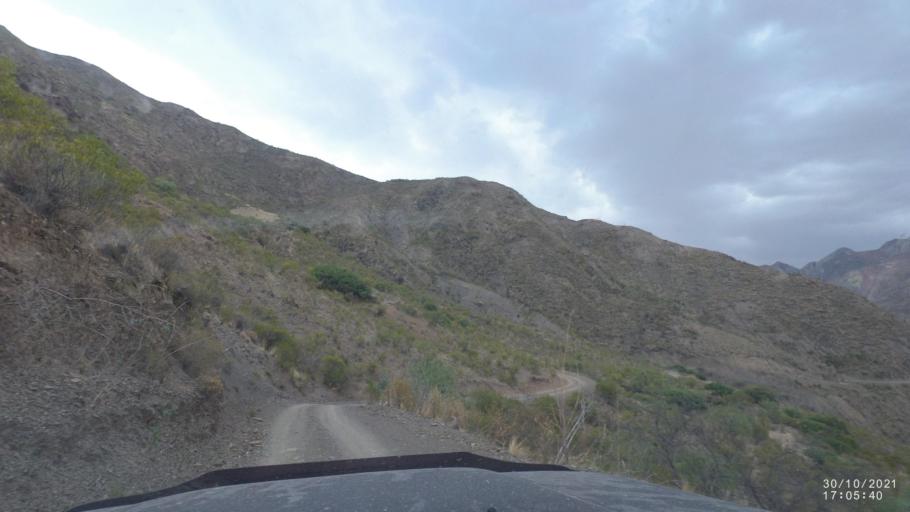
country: BO
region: Cochabamba
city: Colchani
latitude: -17.5664
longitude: -66.6283
